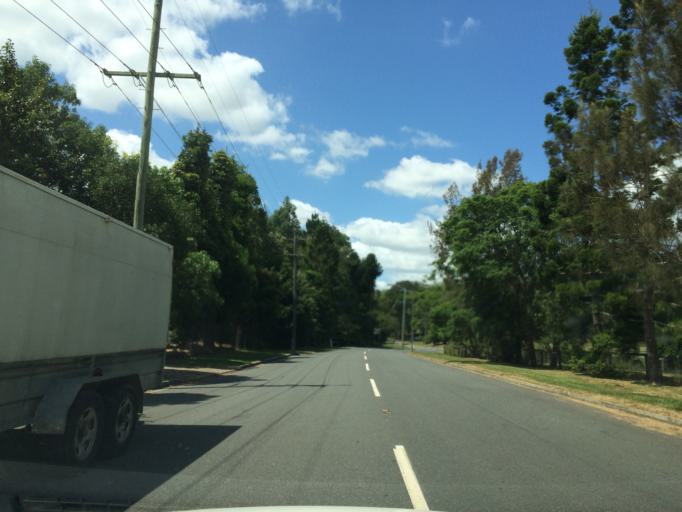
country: AU
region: Queensland
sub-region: Brisbane
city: Kenmore Hills
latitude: -27.4953
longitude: 152.9095
